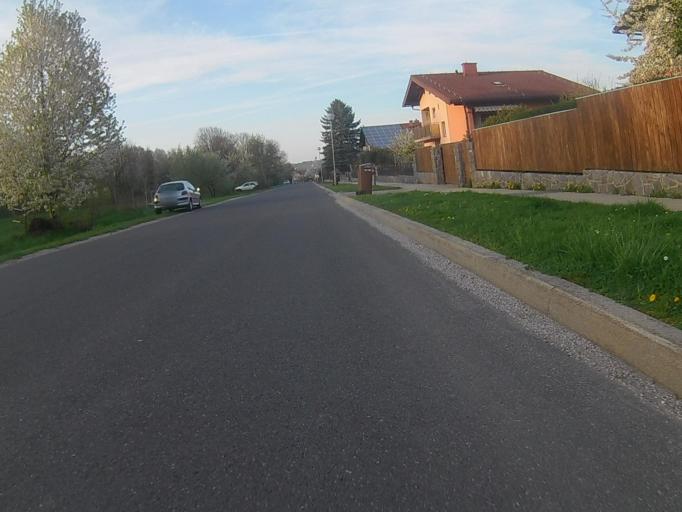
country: SI
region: Maribor
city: Pekre
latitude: 46.5436
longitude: 15.5918
